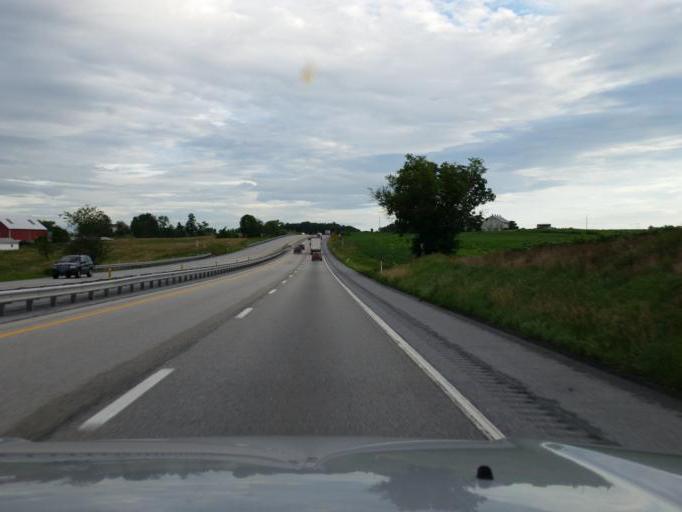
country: US
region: Pennsylvania
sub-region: Adams County
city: Lake Meade
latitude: 40.0417
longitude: -77.0753
